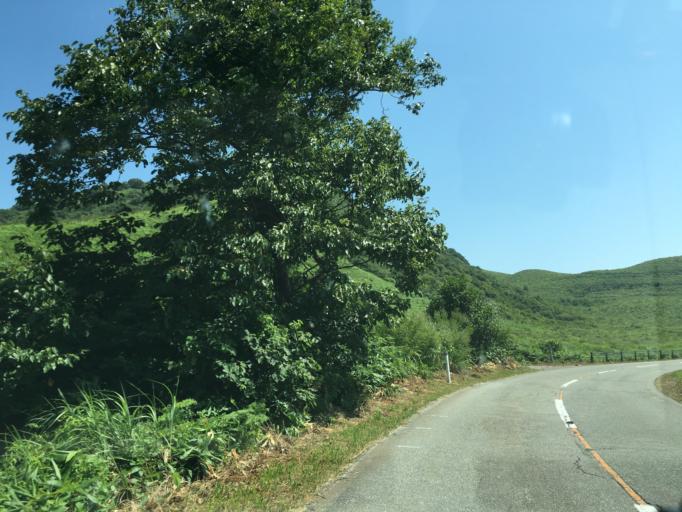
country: JP
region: Akita
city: Tenno
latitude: 39.9383
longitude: 139.8714
